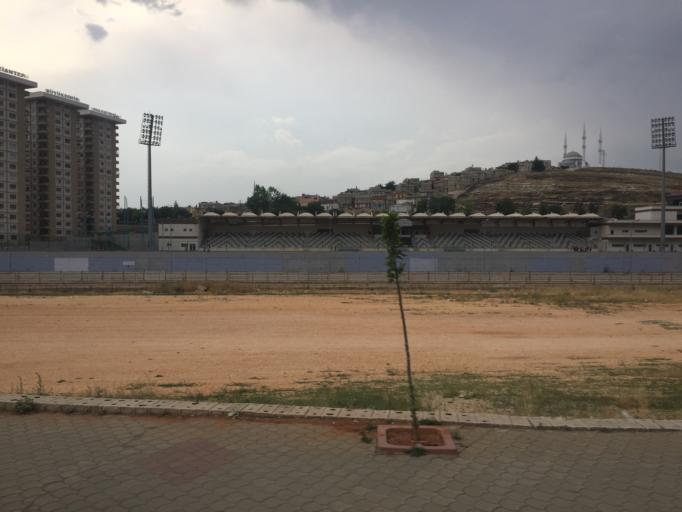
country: TR
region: Gaziantep
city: Gaziantep
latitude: 37.0748
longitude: 37.4129
